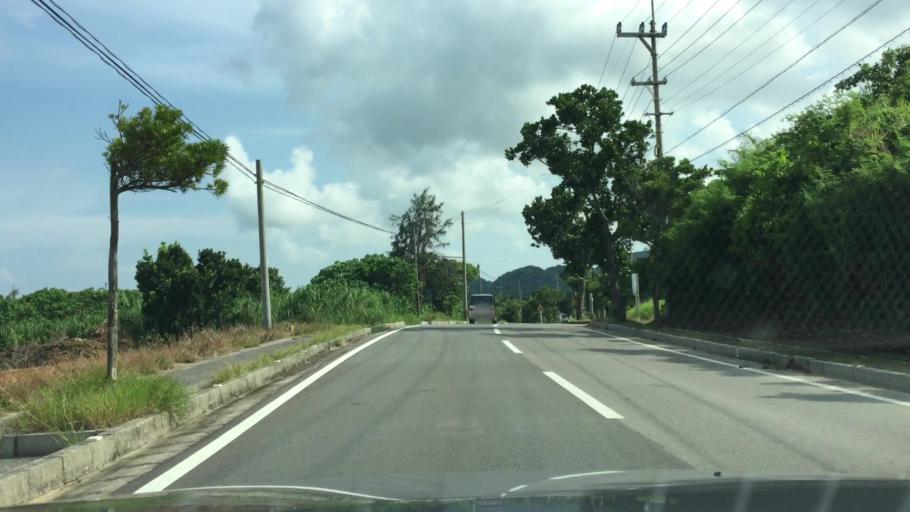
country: JP
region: Okinawa
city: Ishigaki
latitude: 24.4608
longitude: 124.2500
